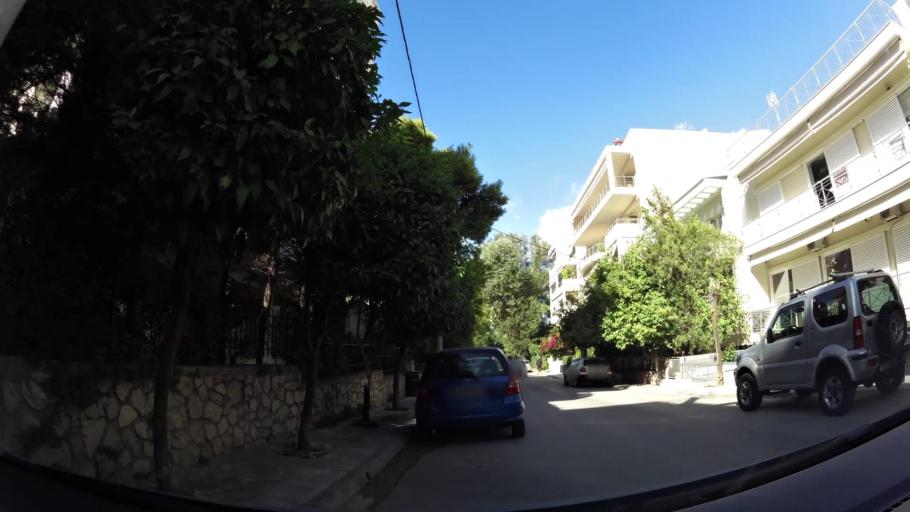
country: GR
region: Attica
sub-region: Nomarchia Athinas
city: Neo Psychiko
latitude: 38.0075
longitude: 23.7809
